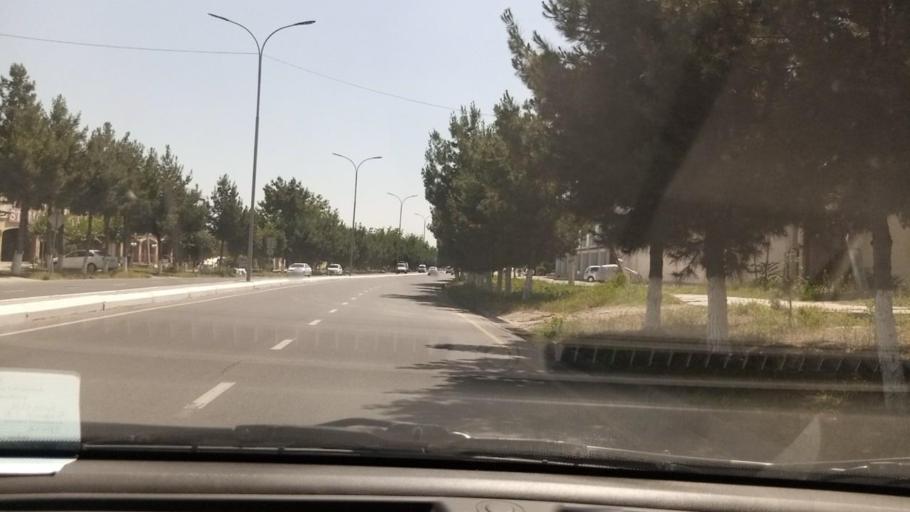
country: UZ
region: Toshkent
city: Urtaowul
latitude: 41.2182
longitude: 69.1745
